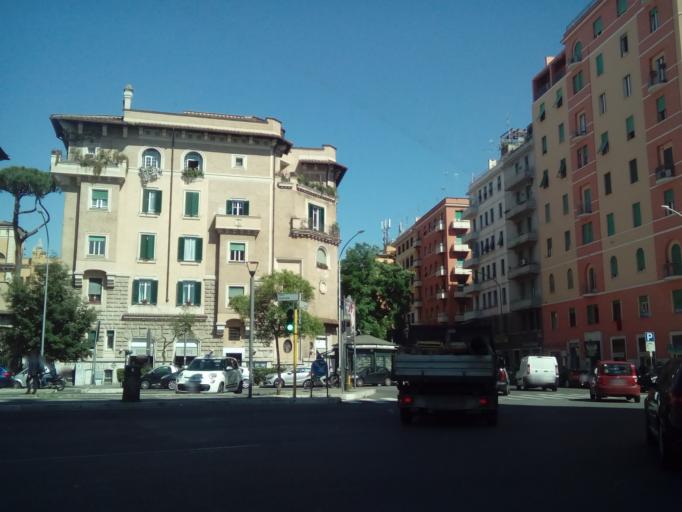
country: IT
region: Latium
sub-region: Citta metropolitana di Roma Capitale
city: Rome
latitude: 41.8803
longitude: 12.5079
